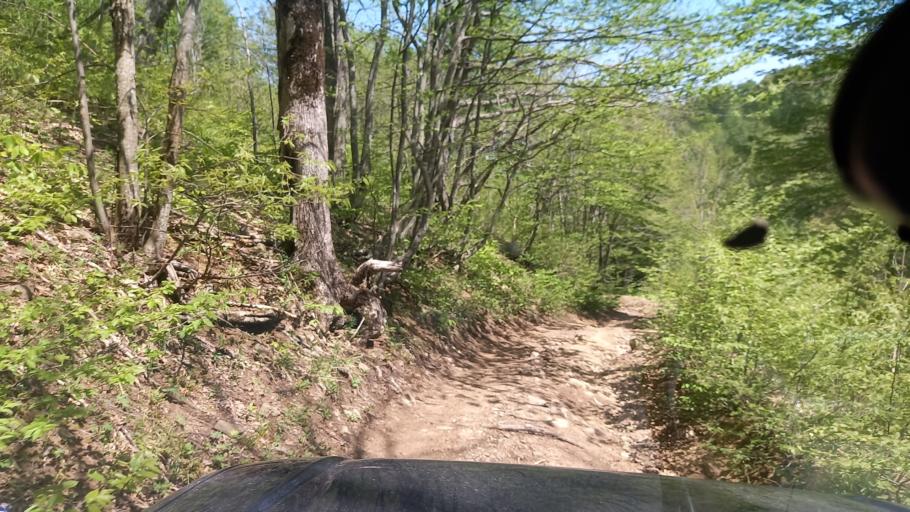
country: RU
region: Krasnodarskiy
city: Tuapse
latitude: 44.2456
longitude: 39.2954
